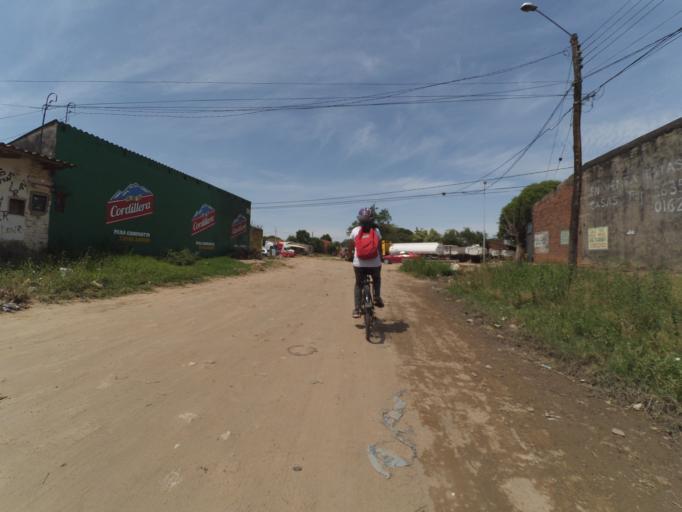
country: BO
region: Santa Cruz
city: Santa Cruz de la Sierra
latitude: -17.8289
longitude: -63.2324
